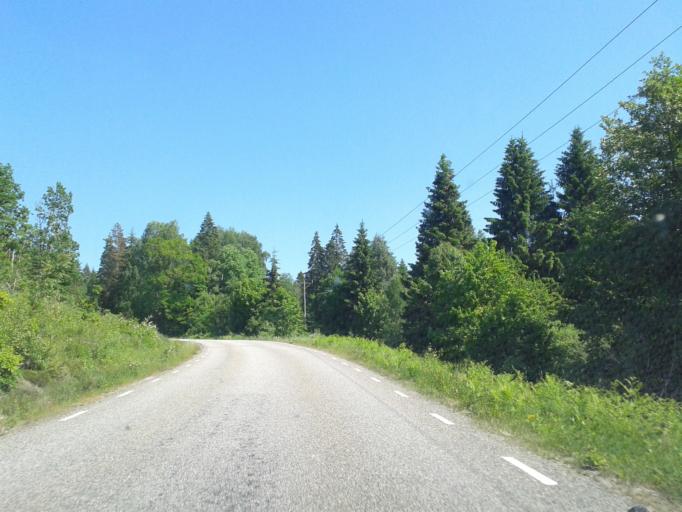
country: SE
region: Vaestra Goetaland
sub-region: Kungalvs Kommun
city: Diserod
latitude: 57.9756
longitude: 11.9590
